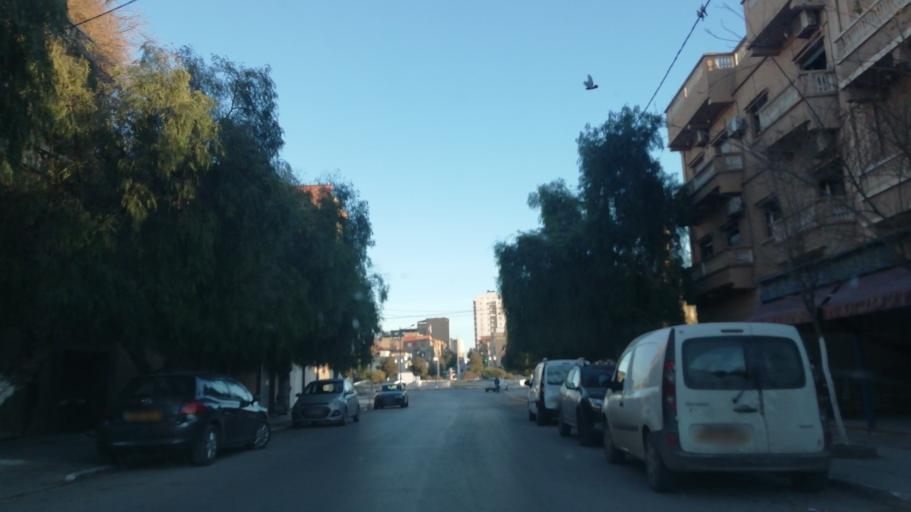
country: DZ
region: Oran
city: Bir el Djir
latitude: 35.7303
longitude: -0.5811
